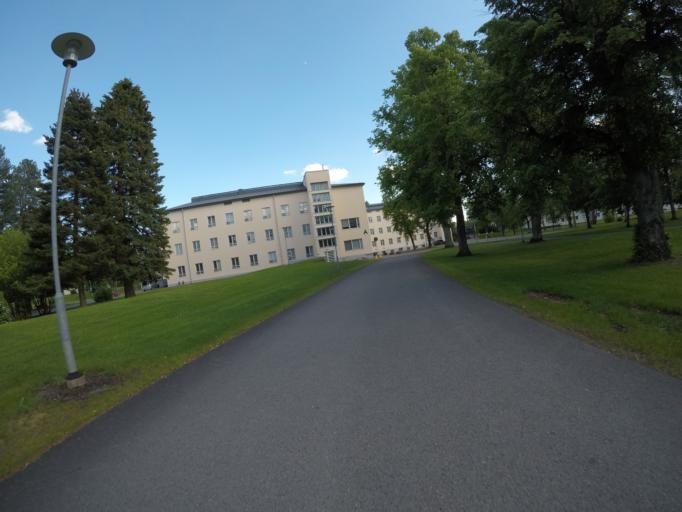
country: FI
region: Haeme
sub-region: Haemeenlinna
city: Haemeenlinna
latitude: 60.9769
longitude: 24.4757
